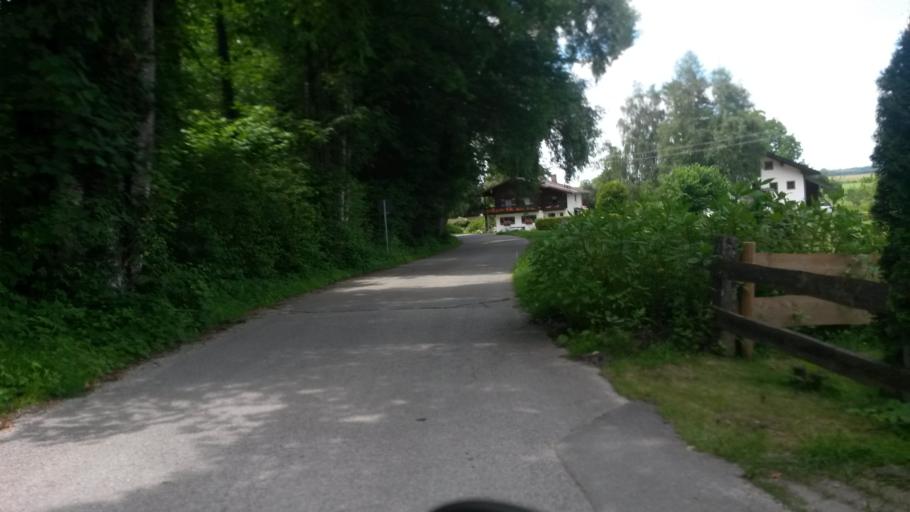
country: DE
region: Bavaria
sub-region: Upper Bavaria
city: Ubersee
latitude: 47.8132
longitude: 12.4710
